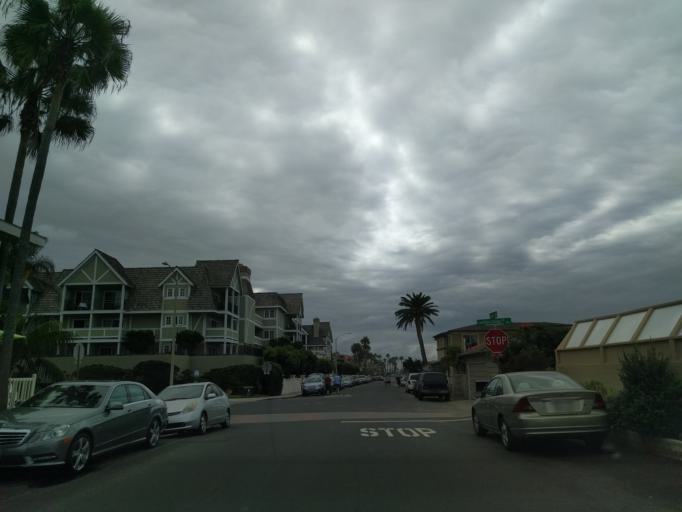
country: US
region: California
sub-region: San Diego County
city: Carlsbad
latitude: 33.1576
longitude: -117.3527
